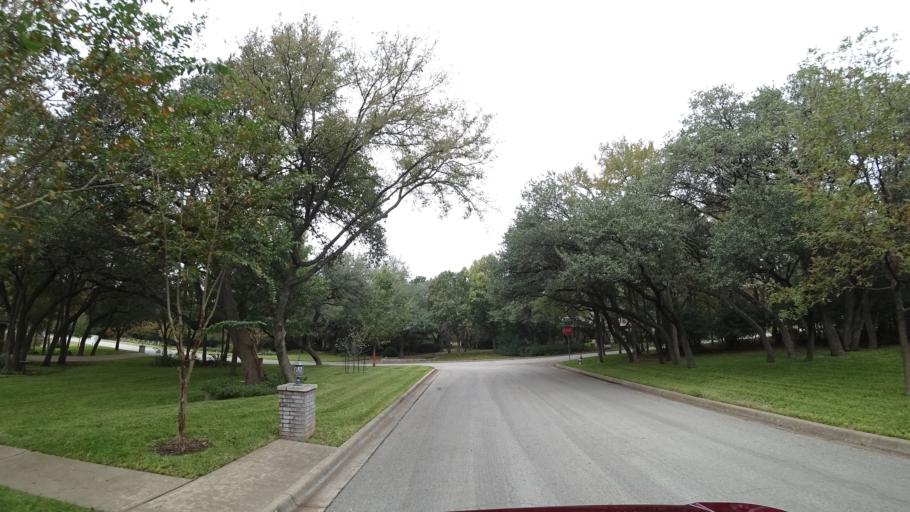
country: US
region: Texas
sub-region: Travis County
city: Wells Branch
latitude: 30.4349
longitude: -97.7157
